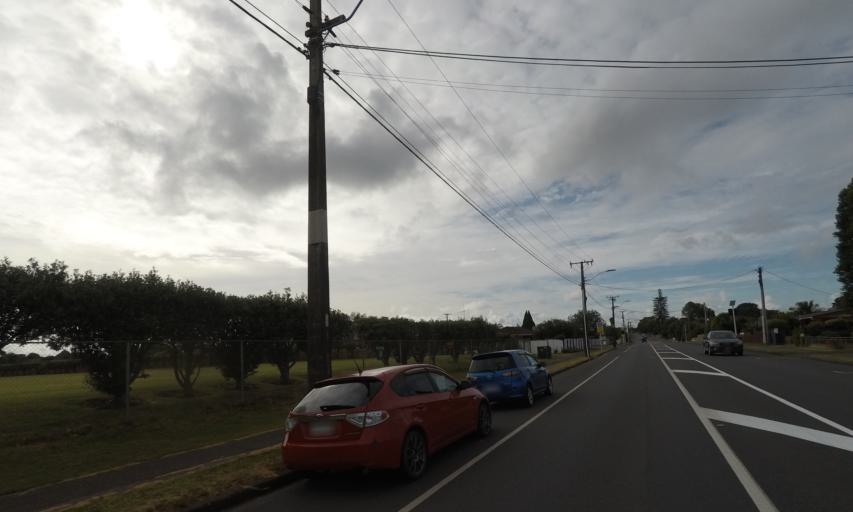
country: NZ
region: Northland
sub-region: Whangarei
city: Whangarei
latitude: -35.6862
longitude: 174.3025
